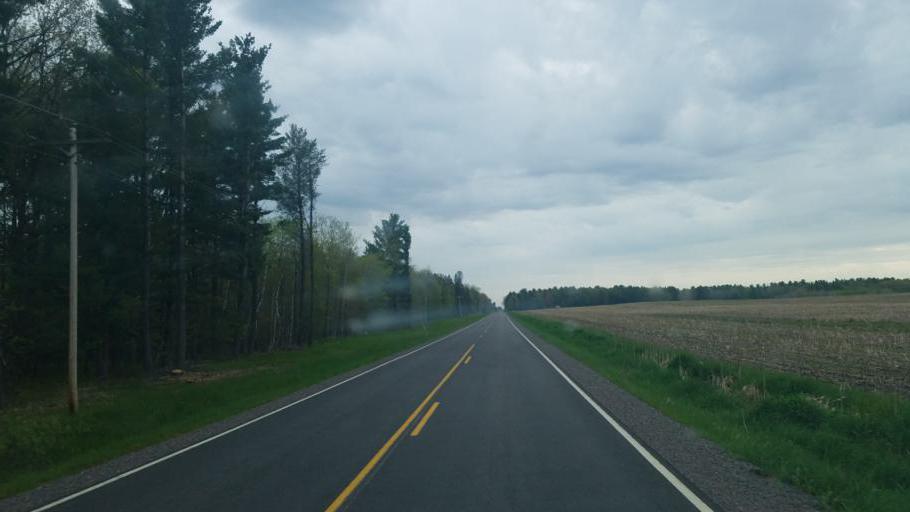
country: US
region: Wisconsin
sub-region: Wood County
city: Marshfield
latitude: 44.4708
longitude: -90.2801
